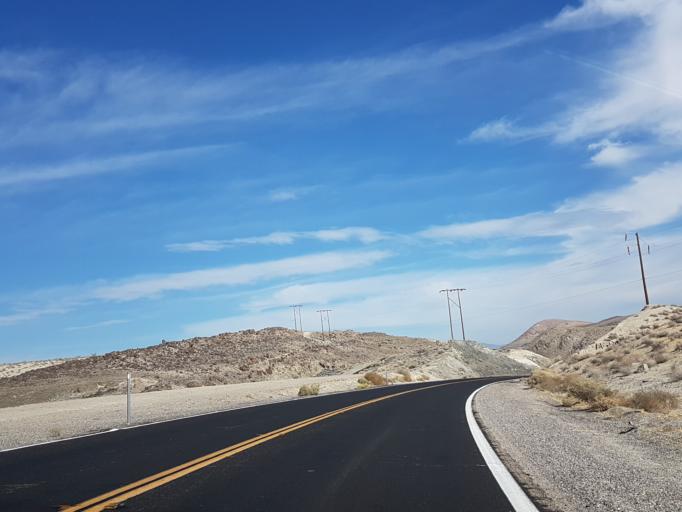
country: US
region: California
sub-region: San Bernardino County
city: Searles Valley
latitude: 35.6547
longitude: -117.4621
